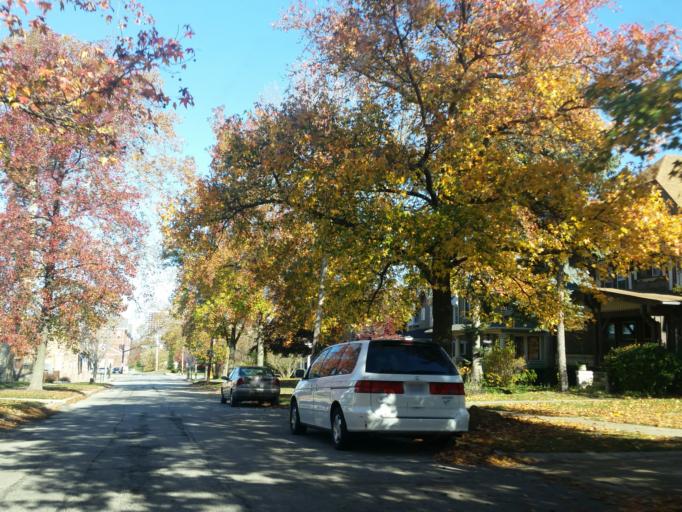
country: US
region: Ohio
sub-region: Cuyahoga County
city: Lakewood
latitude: 41.4831
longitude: -81.7791
